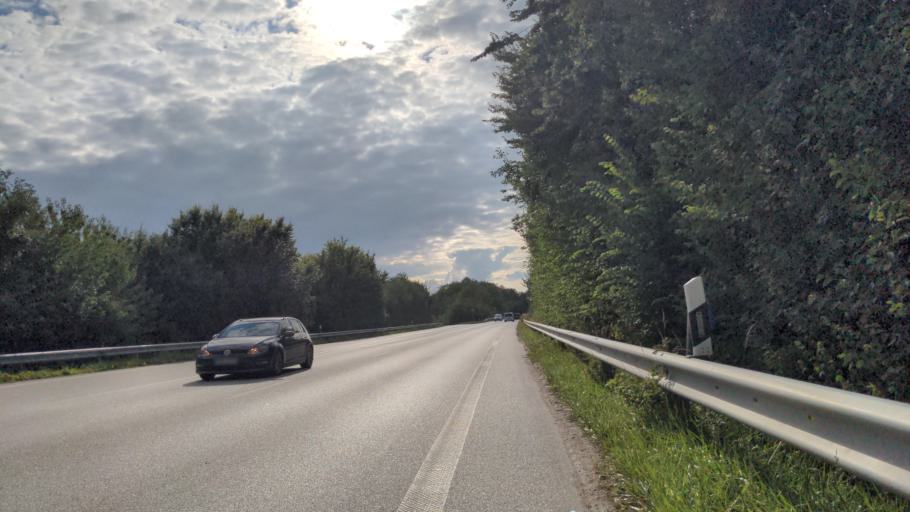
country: DE
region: Schleswig-Holstein
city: Schashagen
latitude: 54.1222
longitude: 10.8619
